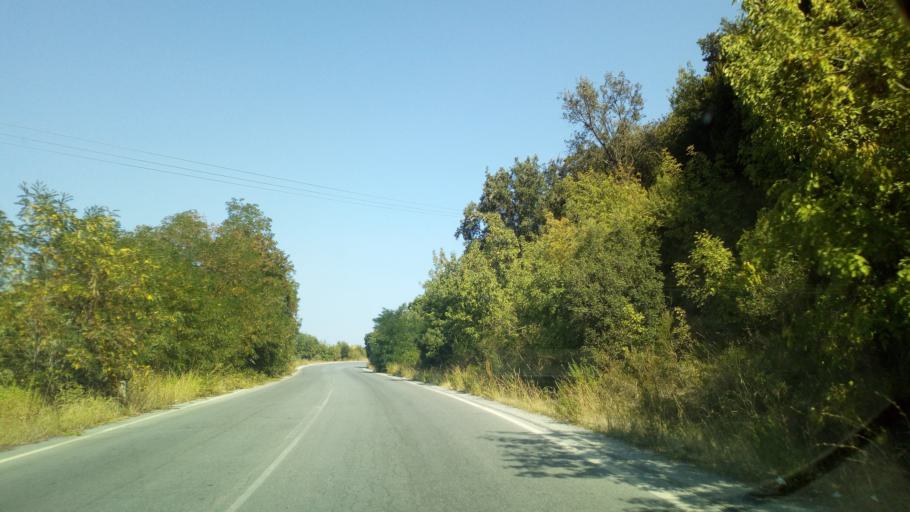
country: GR
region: Central Macedonia
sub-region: Nomos Thessalonikis
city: Stavros
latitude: 40.6551
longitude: 23.7379
